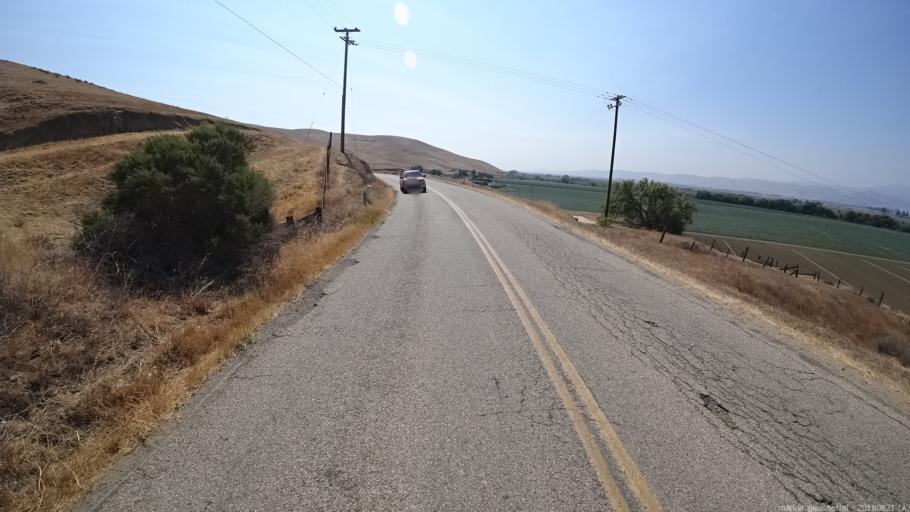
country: US
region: California
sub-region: Monterey County
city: Greenfield
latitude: 36.3825
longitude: -121.2440
